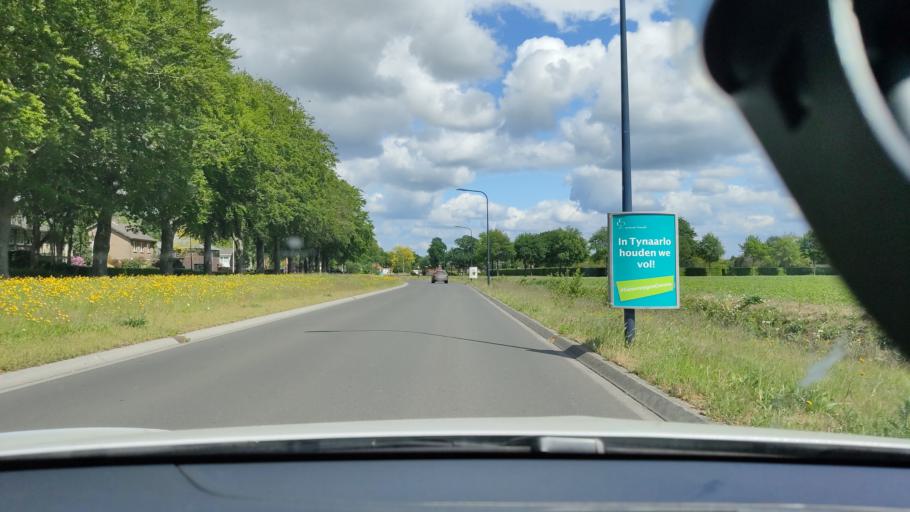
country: NL
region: Drenthe
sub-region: Gemeente Tynaarlo
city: Zuidlaren
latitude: 53.0901
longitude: 6.6860
